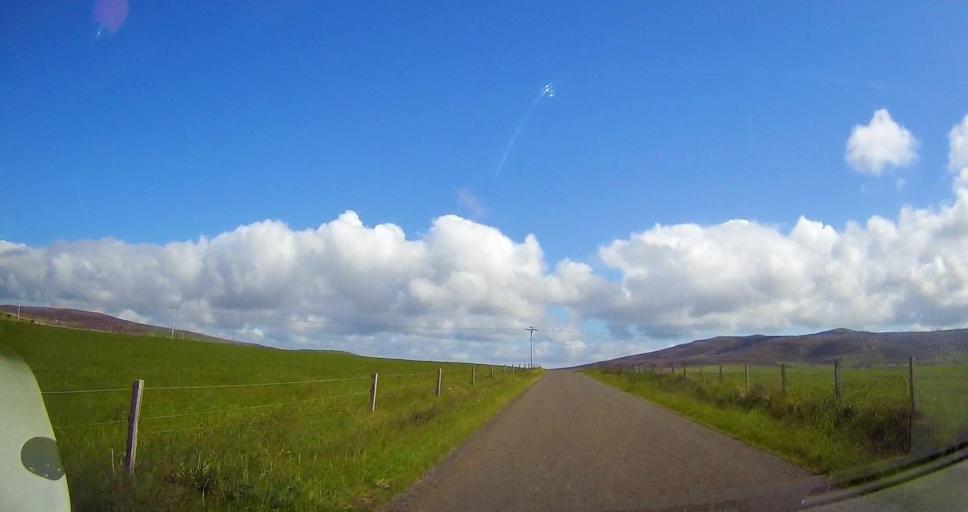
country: GB
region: Scotland
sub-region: Orkney Islands
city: Stromness
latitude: 58.9908
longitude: -3.1558
